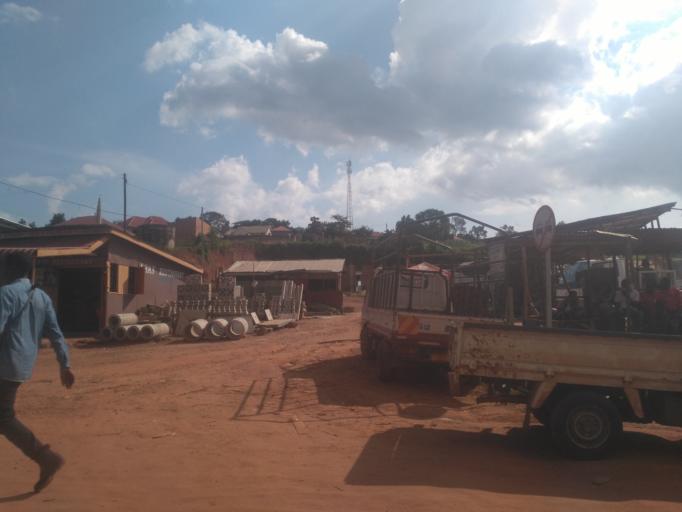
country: UG
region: Central Region
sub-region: Wakiso District
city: Kajansi
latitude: 0.2793
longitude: 32.4722
